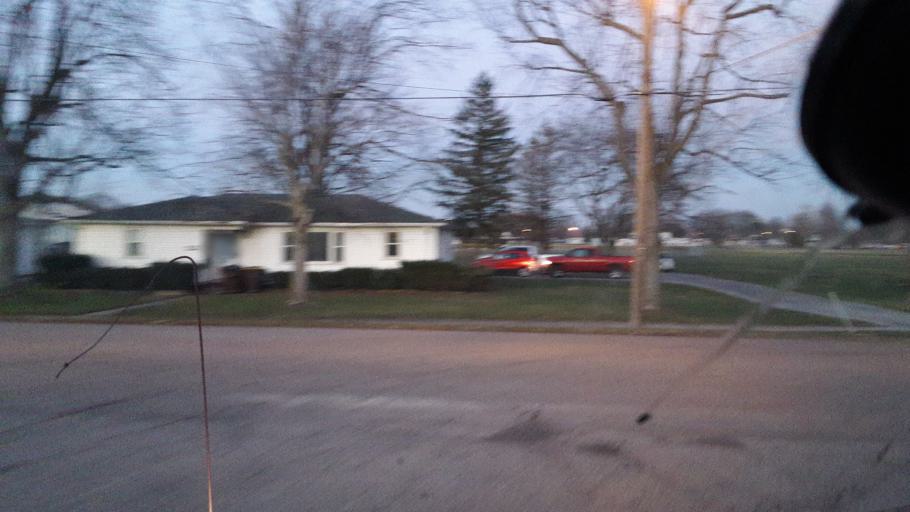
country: US
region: Ohio
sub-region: Defiance County
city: Hicksville
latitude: 41.2938
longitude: -84.7730
